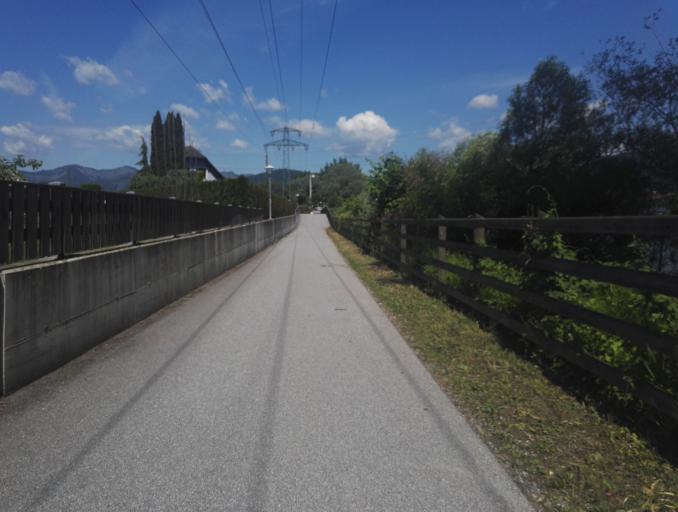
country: AT
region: Styria
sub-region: Politischer Bezirk Graz-Umgebung
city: Gratkorn
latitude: 47.1220
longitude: 15.3479
